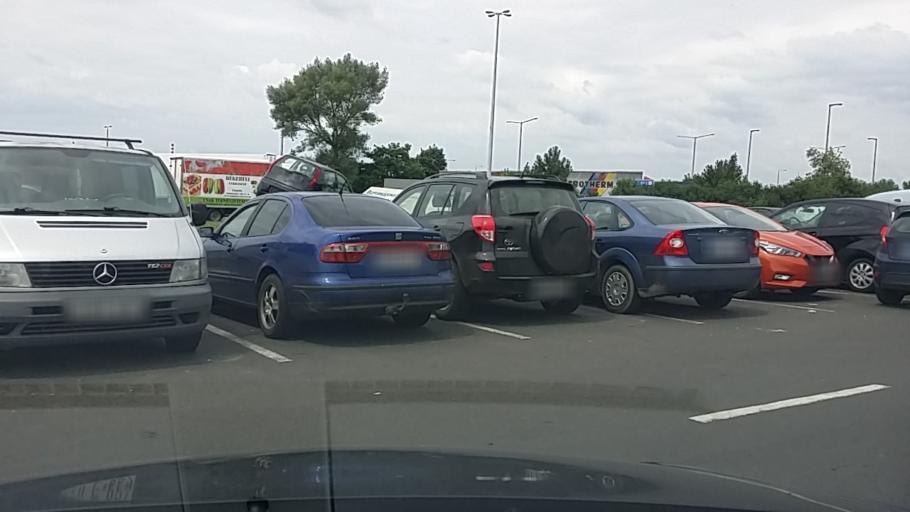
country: HU
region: Budapest
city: Budapest XV. keruelet
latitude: 47.5661
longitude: 19.1475
